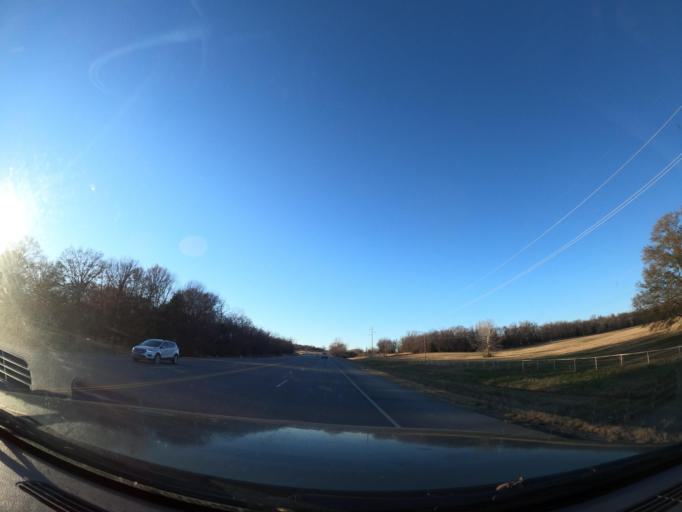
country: US
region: Oklahoma
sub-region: Pittsburg County
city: Hartshorne
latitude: 34.8913
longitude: -95.6207
